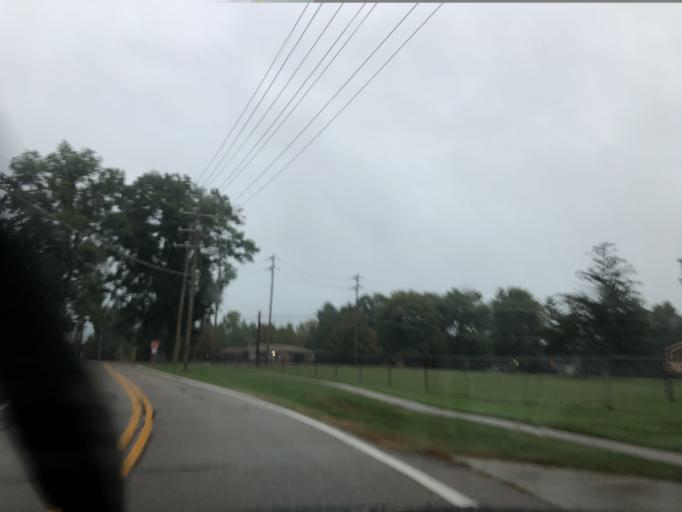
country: US
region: Ohio
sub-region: Hamilton County
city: The Village of Indian Hill
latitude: 39.2355
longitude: -84.3136
